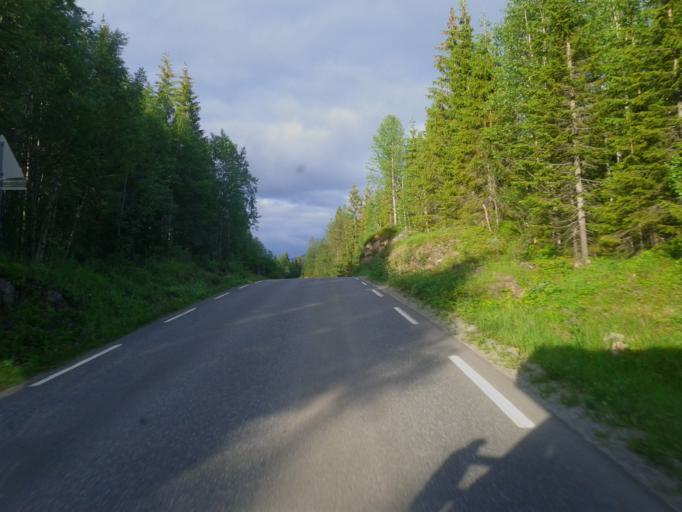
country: NO
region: Nordland
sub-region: Grane
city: Trofors
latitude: 65.5187
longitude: 13.6736
